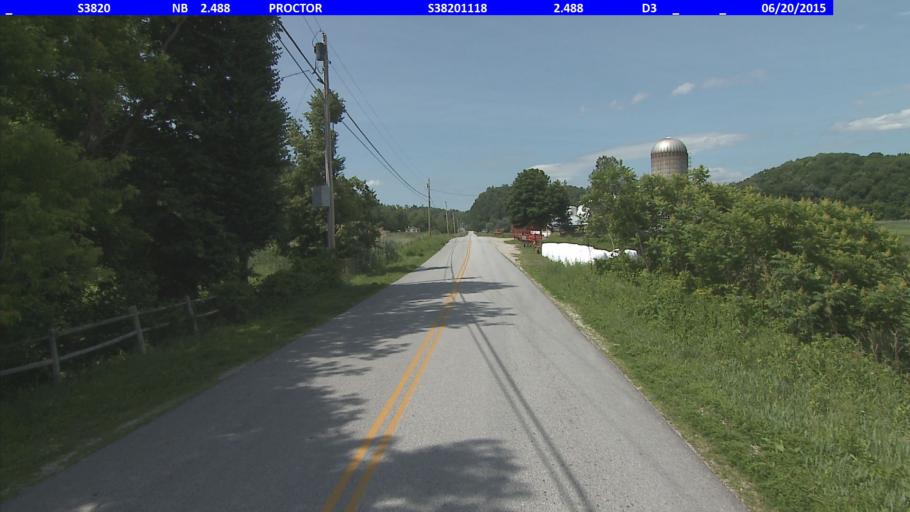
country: US
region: Vermont
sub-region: Rutland County
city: West Rutland
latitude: 43.6445
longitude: -73.0420
